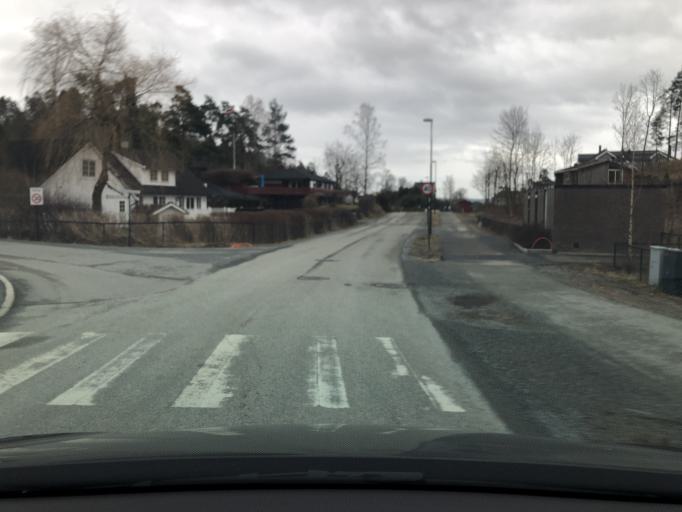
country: NO
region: Akershus
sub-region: Baerum
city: Sandvika
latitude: 59.8608
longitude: 10.5155
